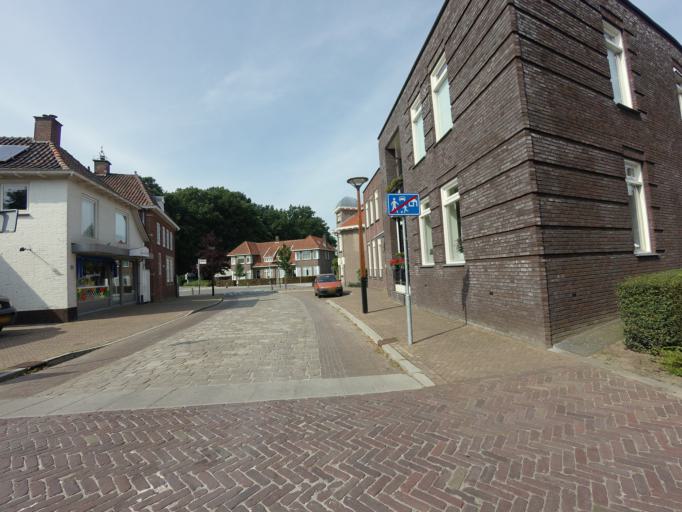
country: NL
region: Overijssel
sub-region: Gemeente Tubbergen
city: Tubbergen
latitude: 52.4088
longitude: 6.7817
